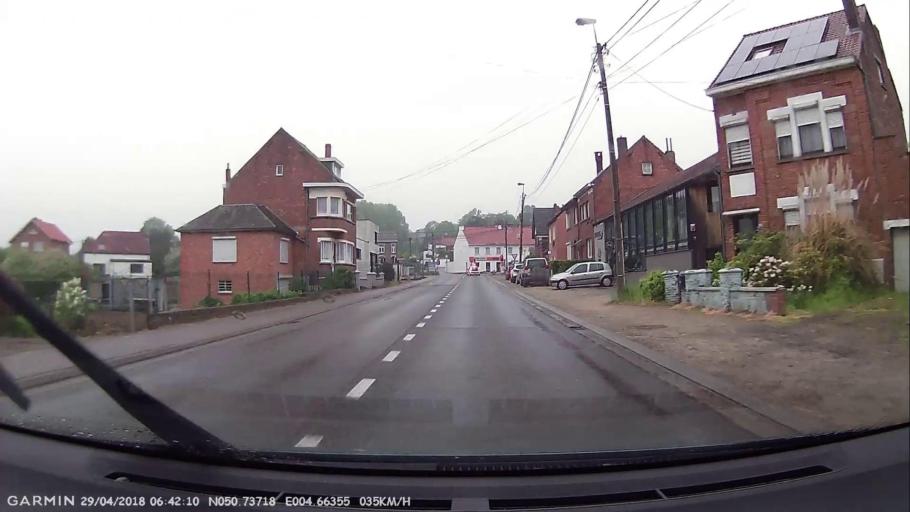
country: BE
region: Wallonia
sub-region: Province du Brabant Wallon
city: Grez-Doiceau
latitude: 50.7373
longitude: 4.6635
